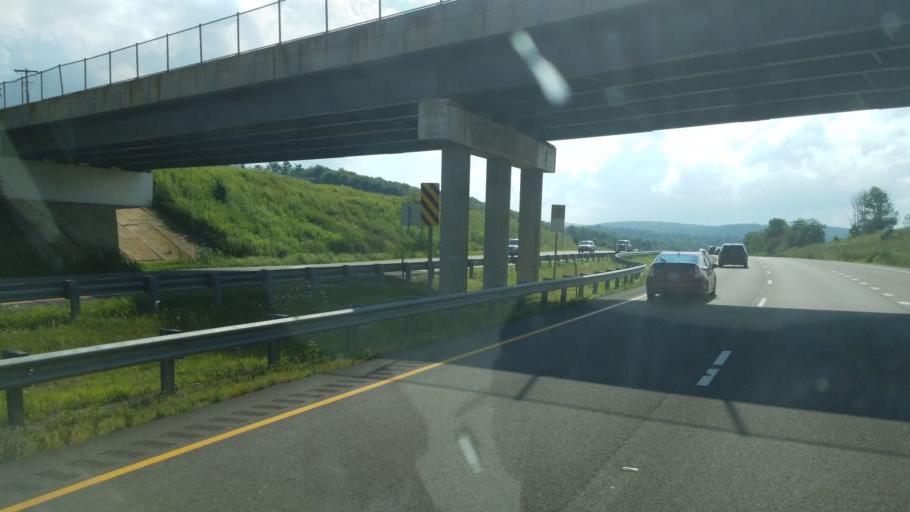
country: US
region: Maryland
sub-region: Allegany County
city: Frostburg
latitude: 39.6830
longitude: -79.0376
